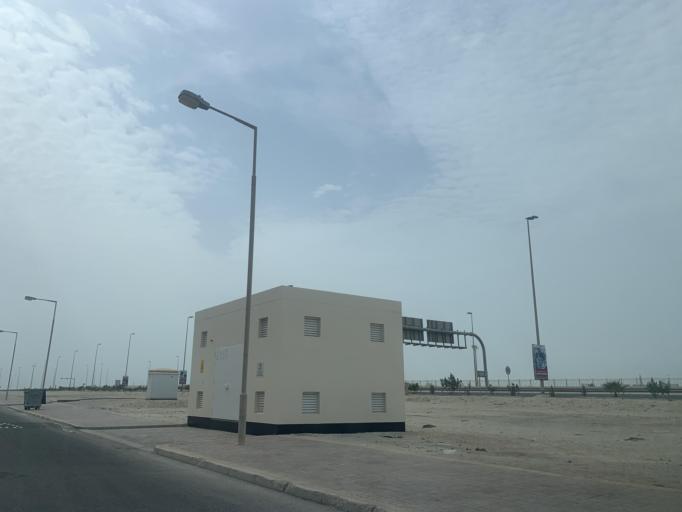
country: BH
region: Muharraq
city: Al Muharraq
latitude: 26.2852
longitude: 50.6407
